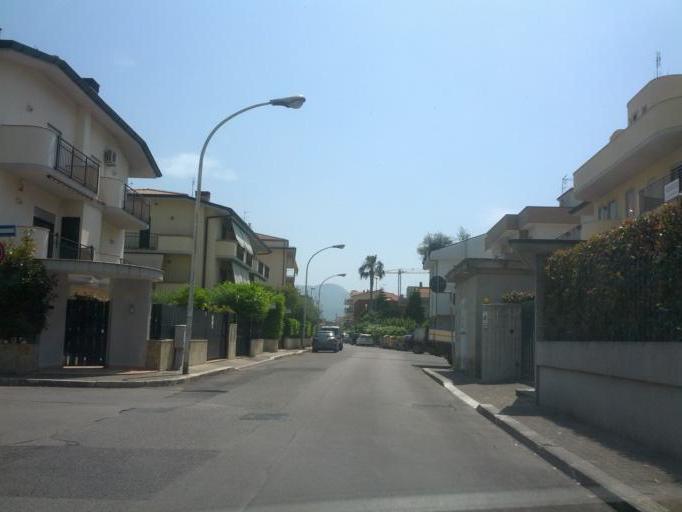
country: IT
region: Latium
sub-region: Provincia di Latina
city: Fondi
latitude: 41.3561
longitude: 13.4238
